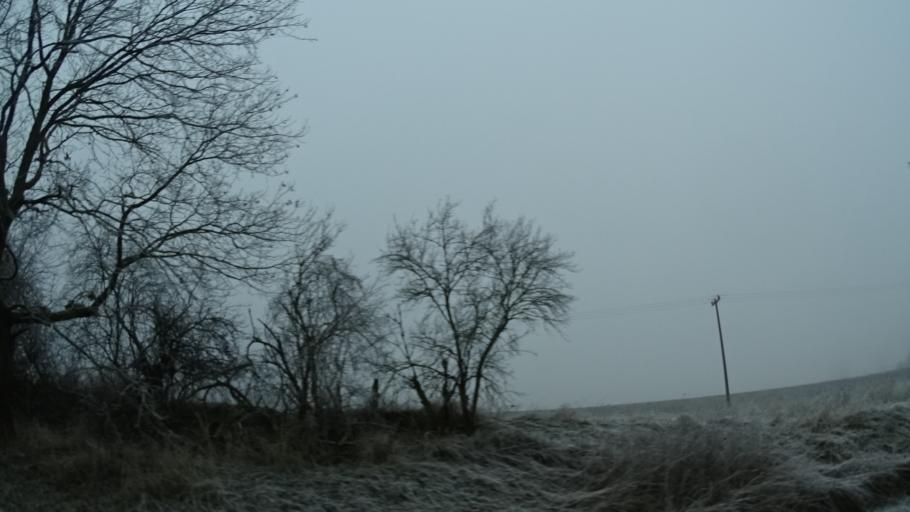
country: DE
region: Bavaria
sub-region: Regierungsbezirk Unterfranken
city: Donnersdorf
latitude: 49.9554
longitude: 10.4260
